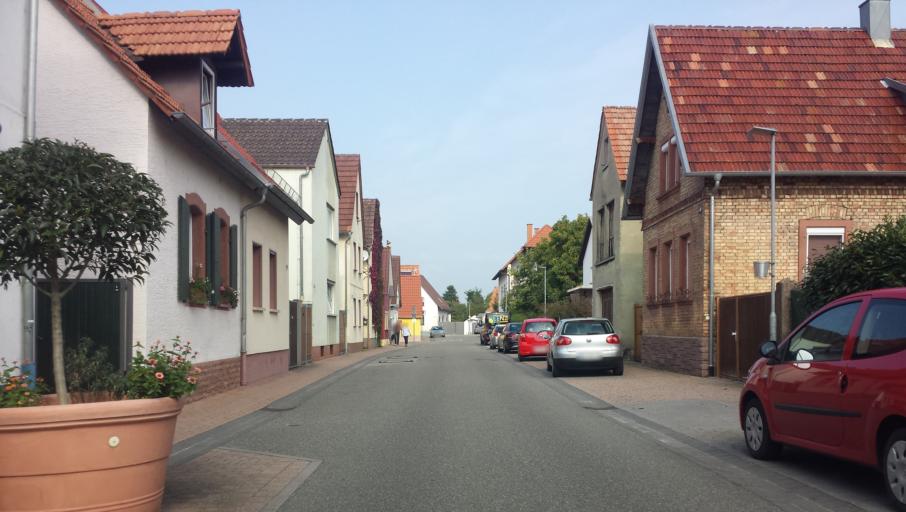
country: DE
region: Rheinland-Pfalz
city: Offenbach an der Queich
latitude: 49.1924
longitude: 8.1937
